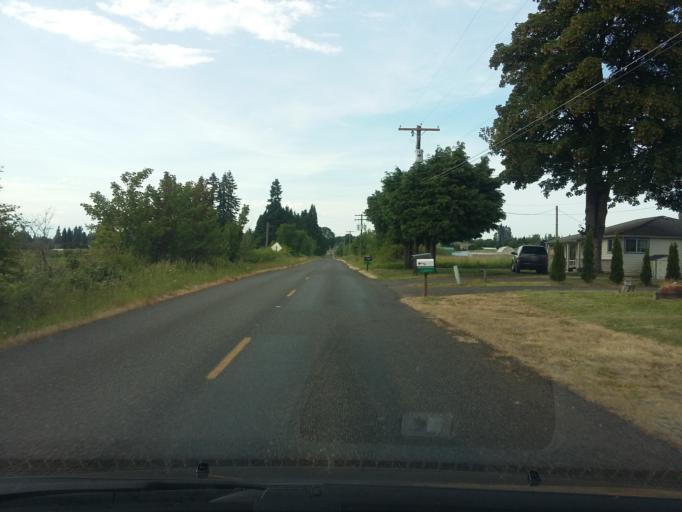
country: US
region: Washington
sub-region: Clark County
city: Barberton
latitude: 45.7108
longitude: -122.5837
